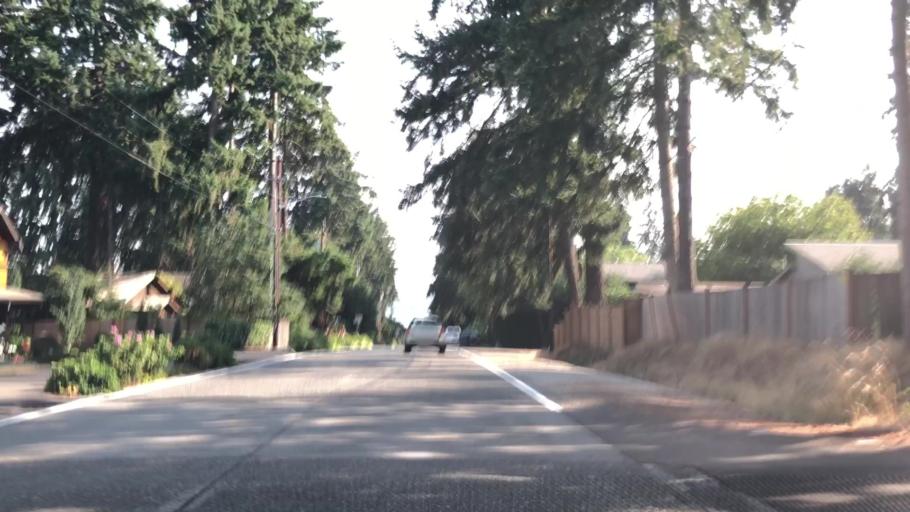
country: US
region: Washington
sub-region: King County
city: Newport
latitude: 47.5838
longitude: -122.1965
